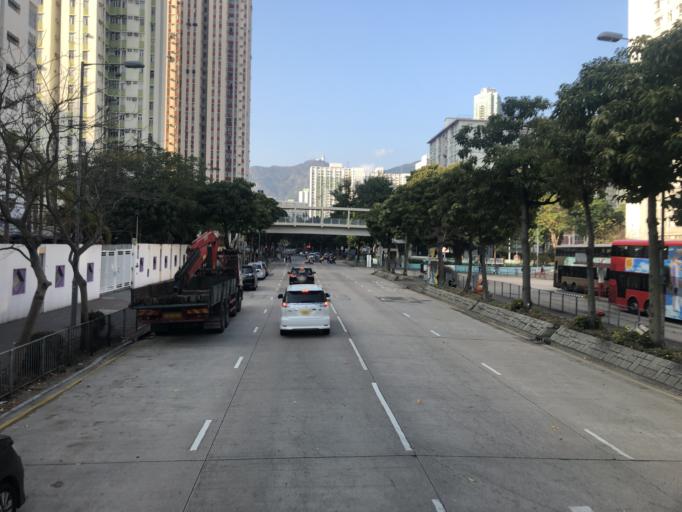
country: HK
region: Kowloon City
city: Kowloon
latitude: 22.3282
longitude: 114.2084
